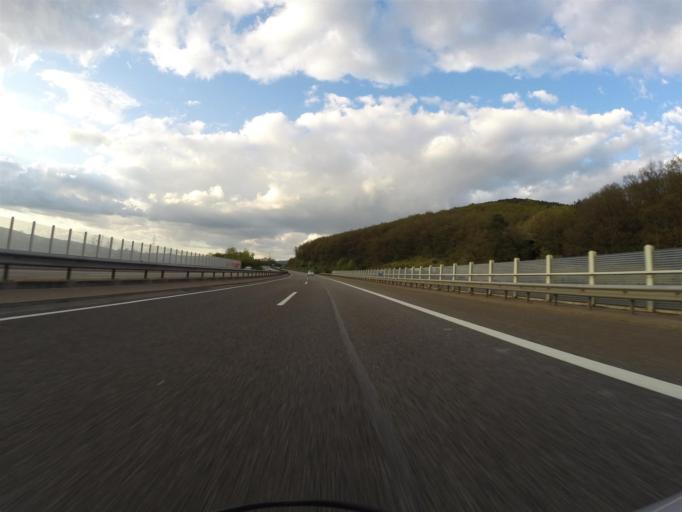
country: DE
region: Rheinland-Pfalz
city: Wartenberg-Rohrbach
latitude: 49.5405
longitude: 7.8547
